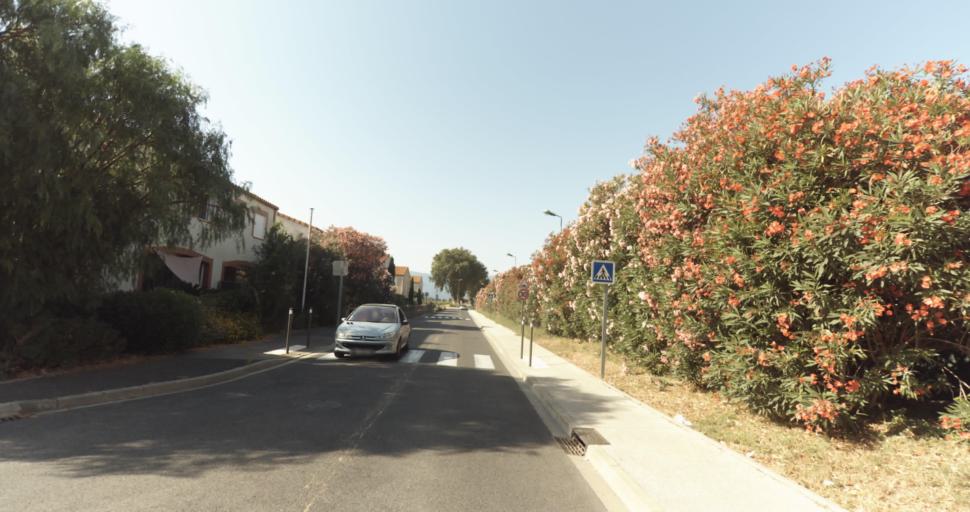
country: FR
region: Languedoc-Roussillon
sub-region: Departement des Pyrenees-Orientales
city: Alenya
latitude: 42.6372
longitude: 2.9816
